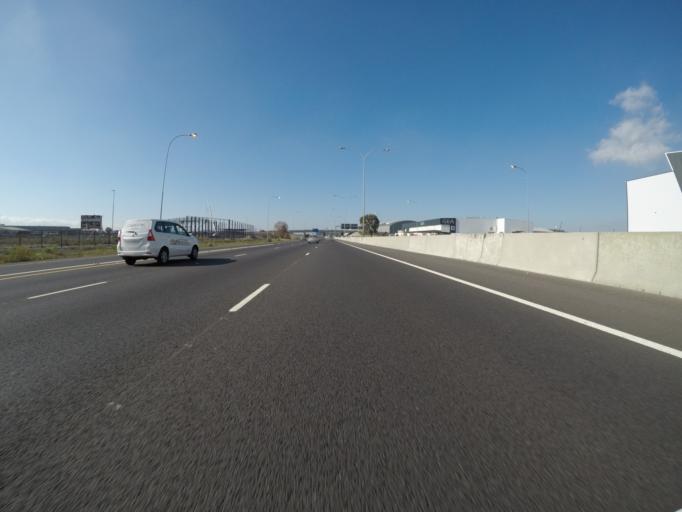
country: ZA
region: Western Cape
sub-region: City of Cape Town
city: Kraaifontein
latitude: -33.9023
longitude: 18.6754
